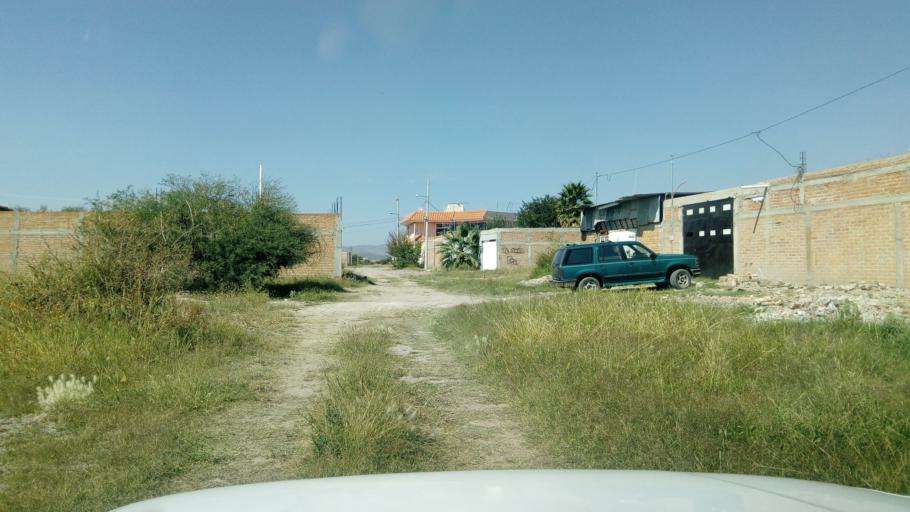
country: MX
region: Durango
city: Victoria de Durango
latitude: 23.9827
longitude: -104.6697
